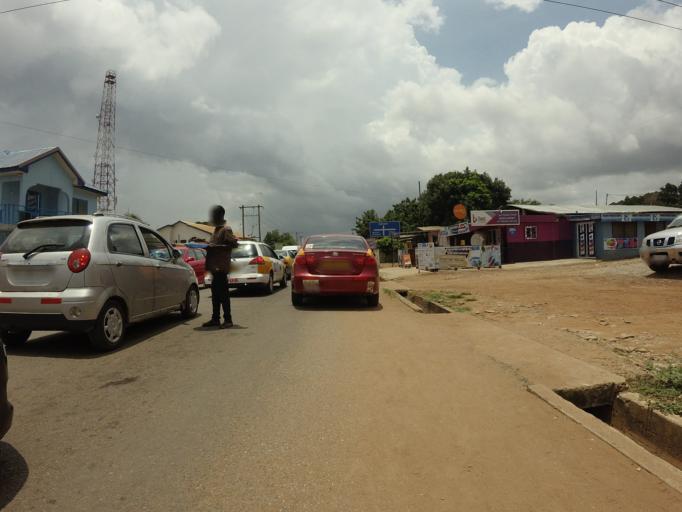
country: GH
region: Greater Accra
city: Medina Estates
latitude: 5.6864
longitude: -0.1695
